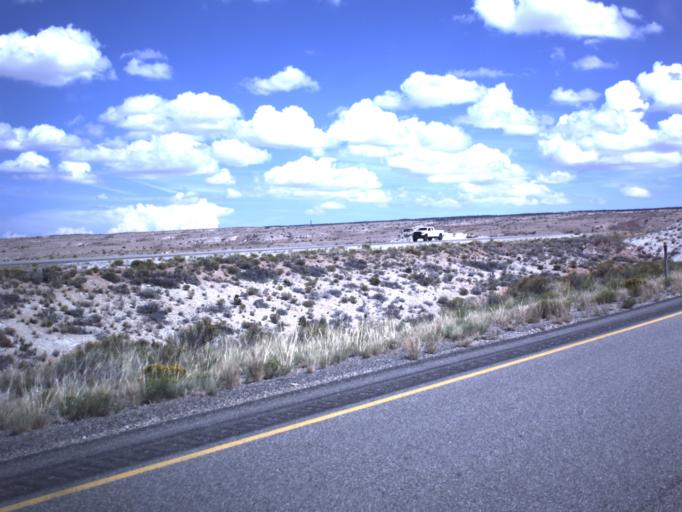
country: US
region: Utah
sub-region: Emery County
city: Ferron
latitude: 38.8448
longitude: -110.9880
